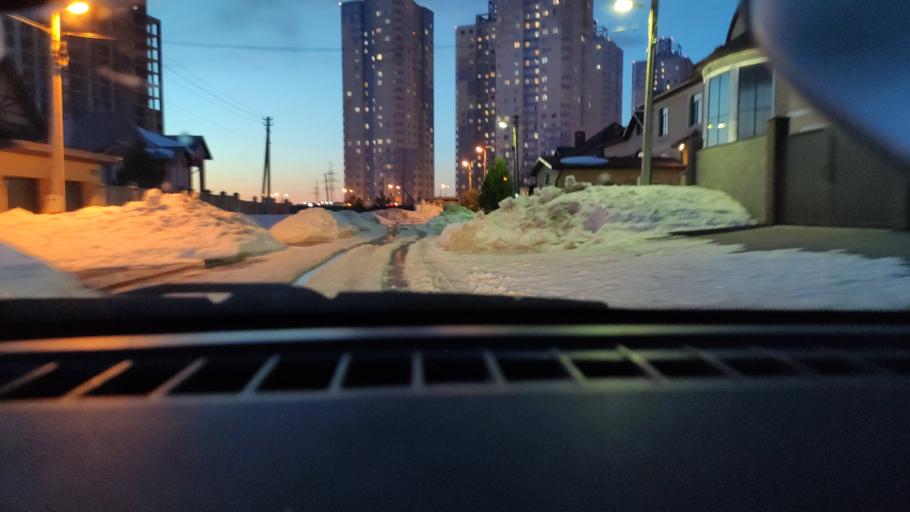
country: RU
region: Perm
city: Perm
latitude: 58.0031
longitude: 56.3232
